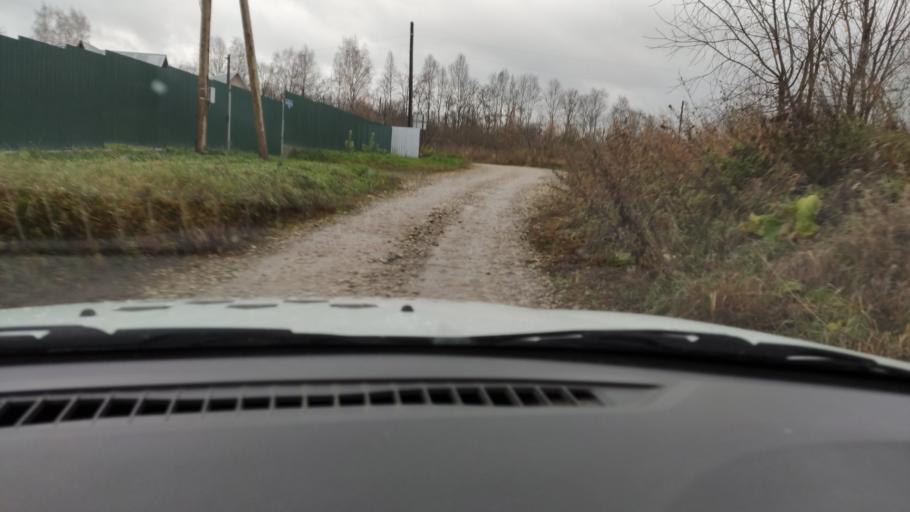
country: RU
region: Perm
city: Sylva
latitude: 58.0465
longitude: 56.7379
